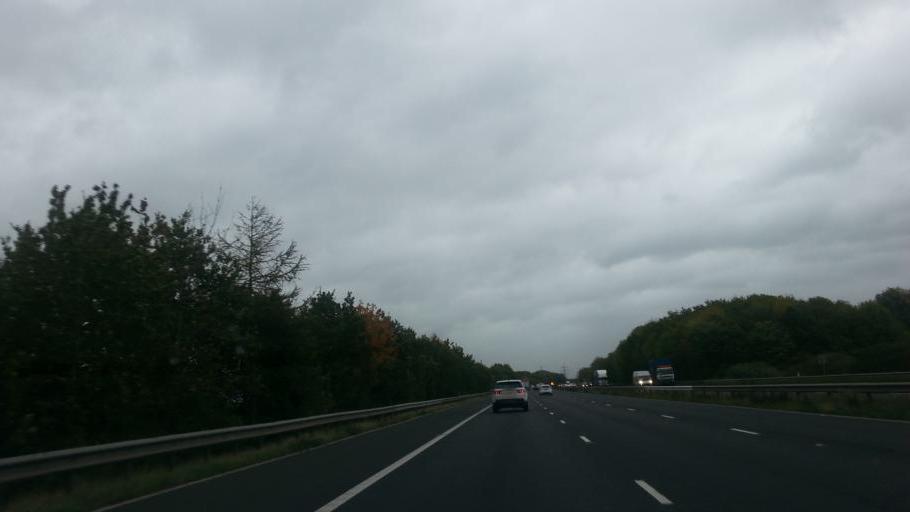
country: GB
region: England
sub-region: Leicestershire
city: Croft
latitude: 52.5797
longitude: -1.2525
